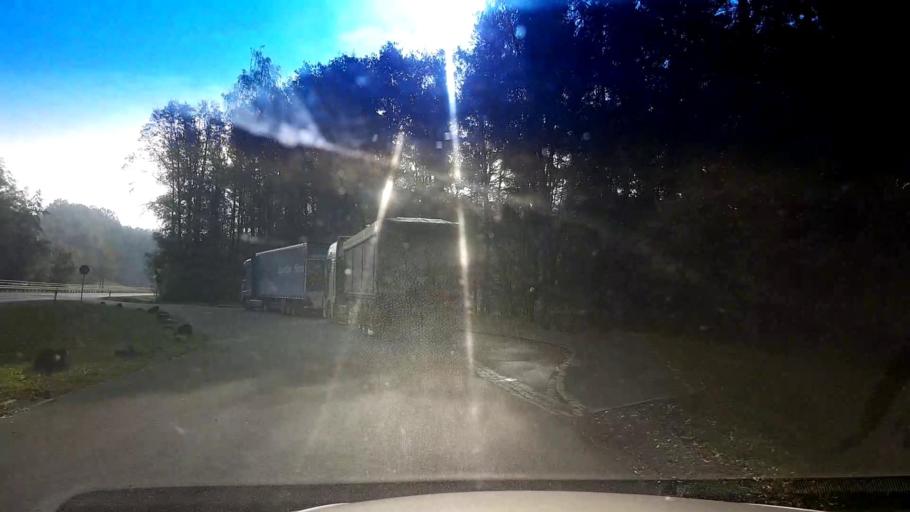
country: DE
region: Bavaria
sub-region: Upper Franconia
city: Neuenmarkt
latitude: 50.1124
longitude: 11.5859
